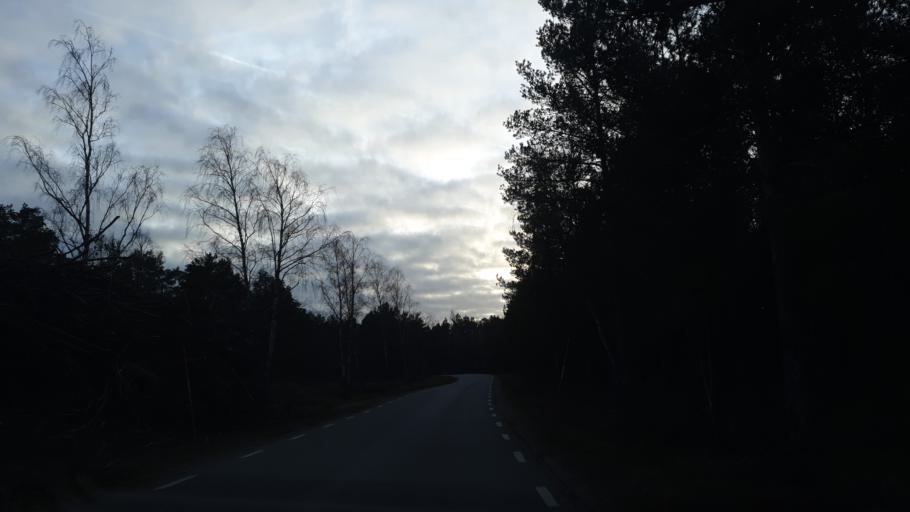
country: SE
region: Blekinge
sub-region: Karlskrona Kommun
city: Jaemjoe
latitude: 56.1388
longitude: 15.8924
